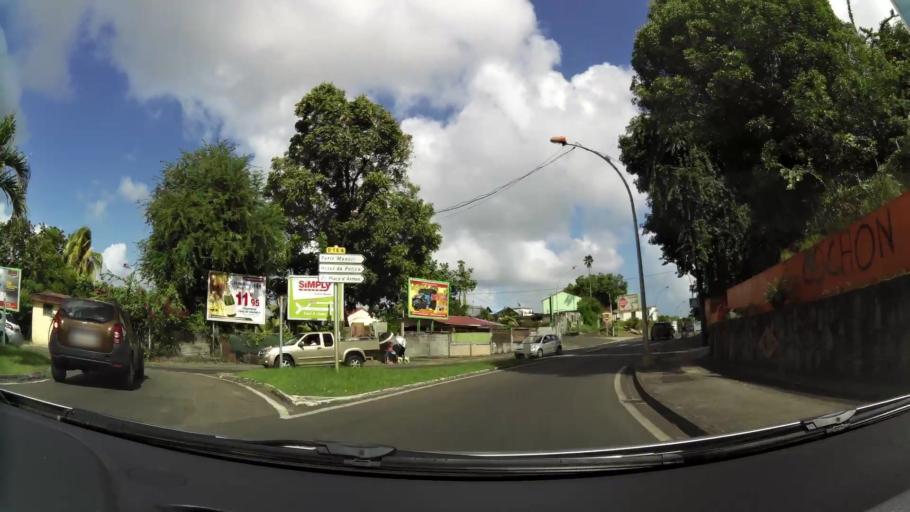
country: MQ
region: Martinique
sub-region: Martinique
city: Le Lamentin
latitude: 14.6105
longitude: -61.0042
